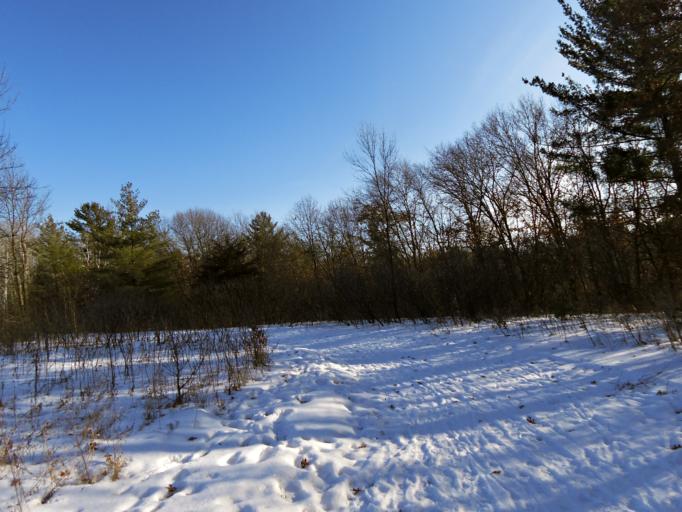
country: US
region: Wisconsin
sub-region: Saint Croix County
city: North Hudson
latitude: 45.0222
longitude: -92.6737
